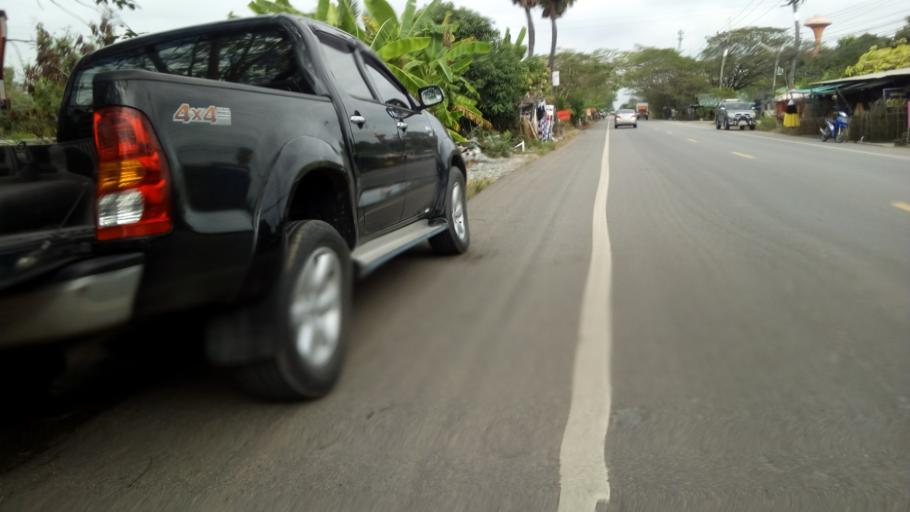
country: TH
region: Pathum Thani
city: Nong Suea
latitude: 14.1945
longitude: 100.8235
